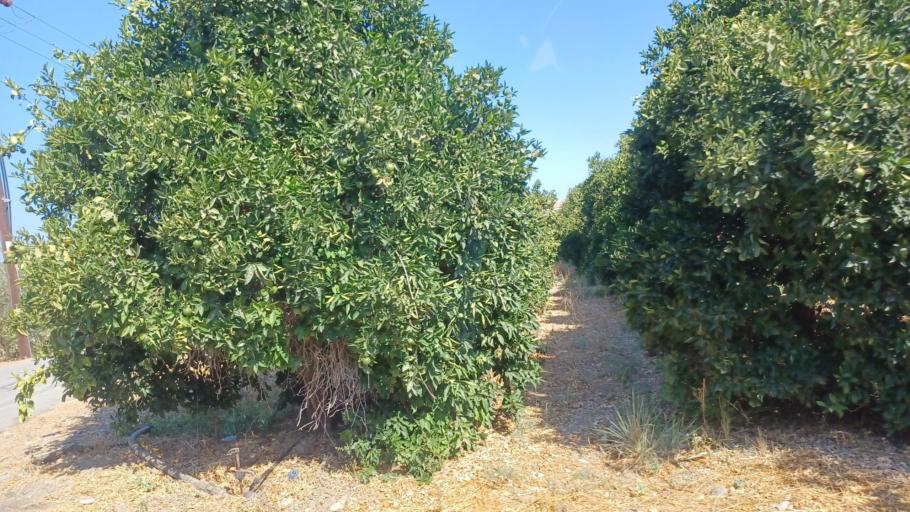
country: CY
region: Pafos
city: Polis
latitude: 35.0406
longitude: 32.4273
